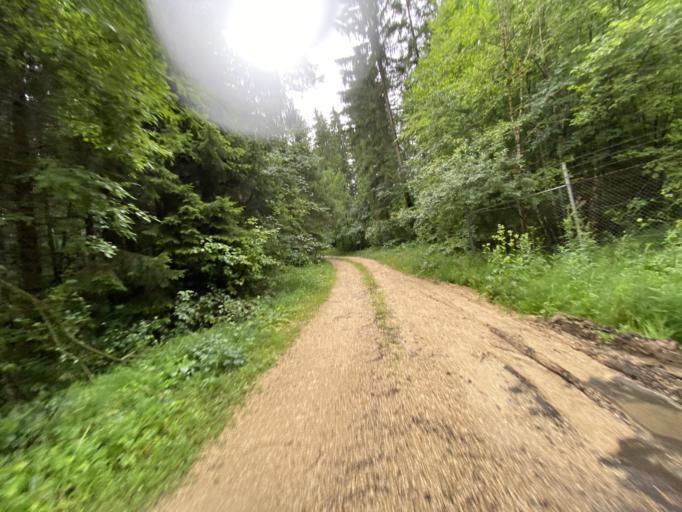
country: DE
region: Baden-Wuerttemberg
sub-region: Tuebingen Region
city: Sigmaringen
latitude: 48.1190
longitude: 9.2343
